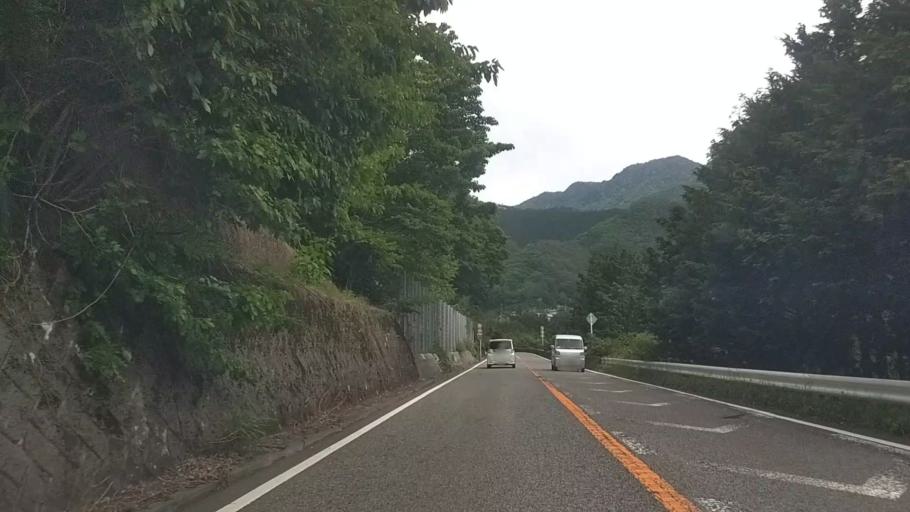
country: JP
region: Yamanashi
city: Fujikawaguchiko
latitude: 35.5305
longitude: 138.6172
